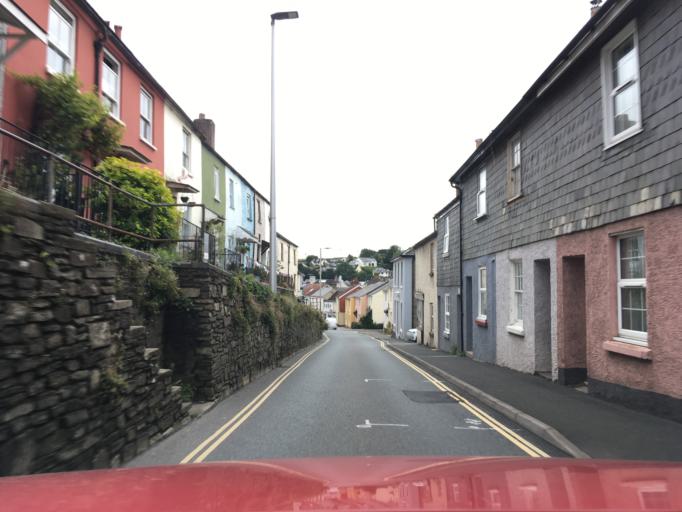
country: GB
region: England
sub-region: Devon
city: Kingsbridge
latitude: 50.2857
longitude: -3.7753
